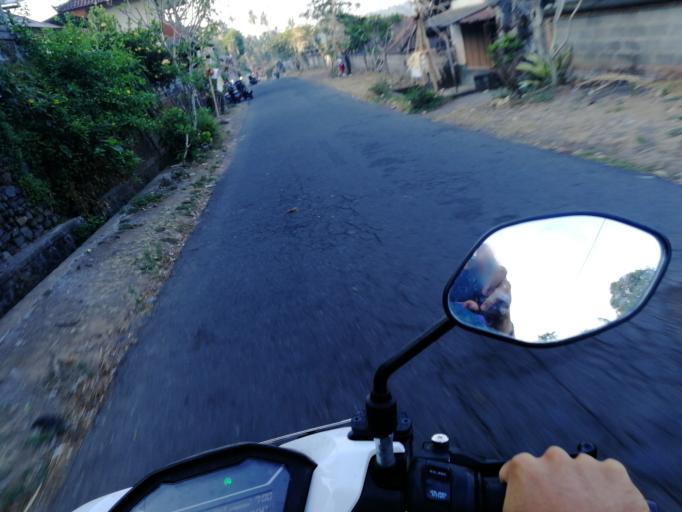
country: ID
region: Bali
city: Tistagede
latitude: -8.3888
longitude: 115.6159
